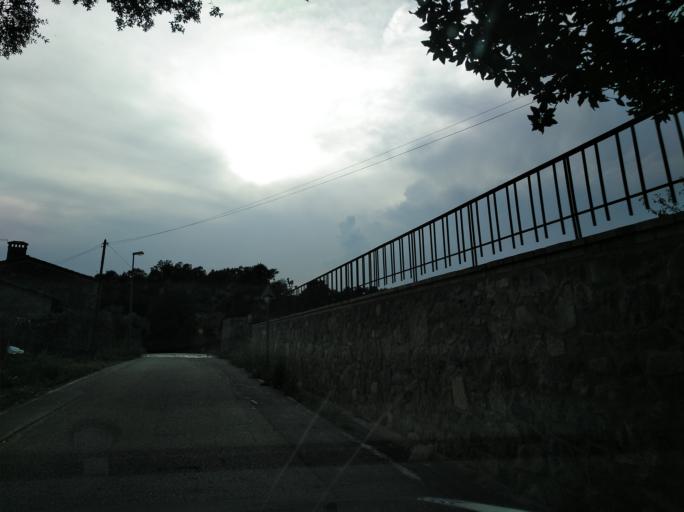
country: ES
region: Catalonia
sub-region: Provincia de Girona
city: Aiguaviva
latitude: 41.9415
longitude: 2.7725
